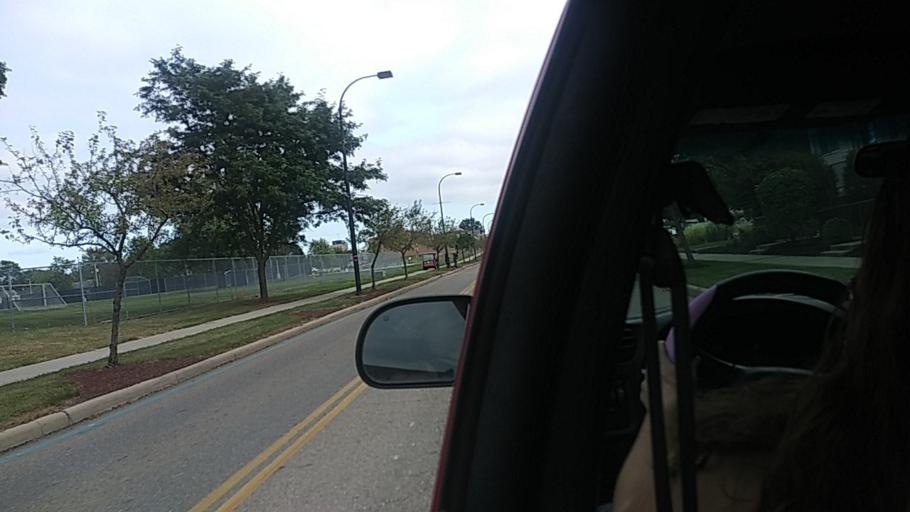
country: US
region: Ohio
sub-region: Summit County
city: Akron
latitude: 41.0689
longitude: -81.5098
